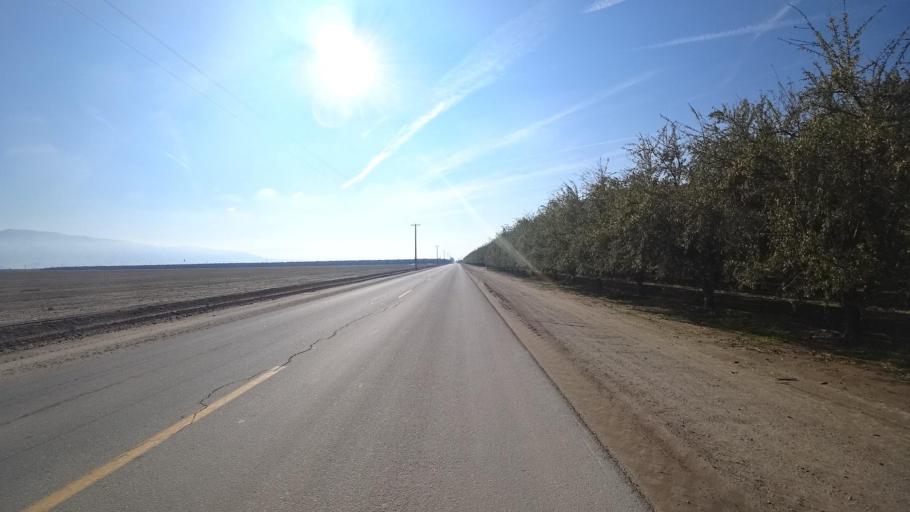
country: US
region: California
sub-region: Kern County
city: Arvin
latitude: 35.2427
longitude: -118.8605
